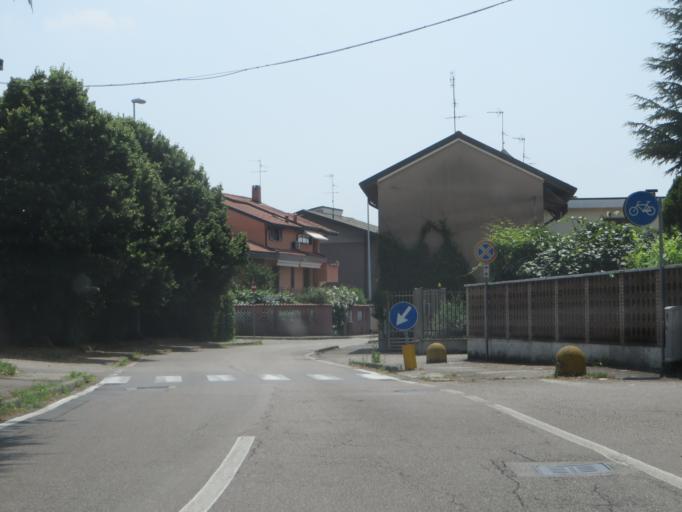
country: IT
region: Lombardy
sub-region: Citta metropolitana di Milano
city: Bareggio
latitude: 45.4835
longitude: 8.9881
